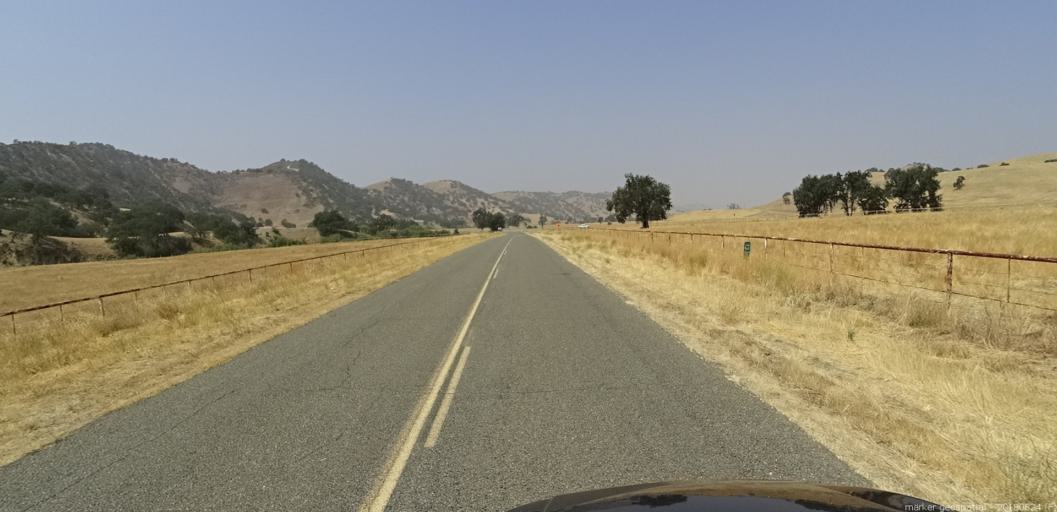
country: US
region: California
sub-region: Monterey County
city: King City
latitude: 36.1866
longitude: -120.8172
